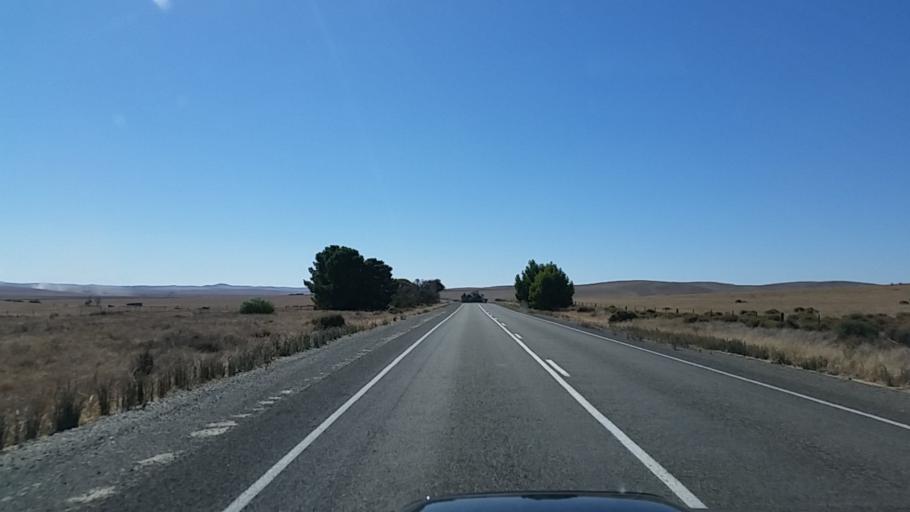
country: AU
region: South Australia
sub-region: Northern Areas
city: Jamestown
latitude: -33.3182
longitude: 138.8832
